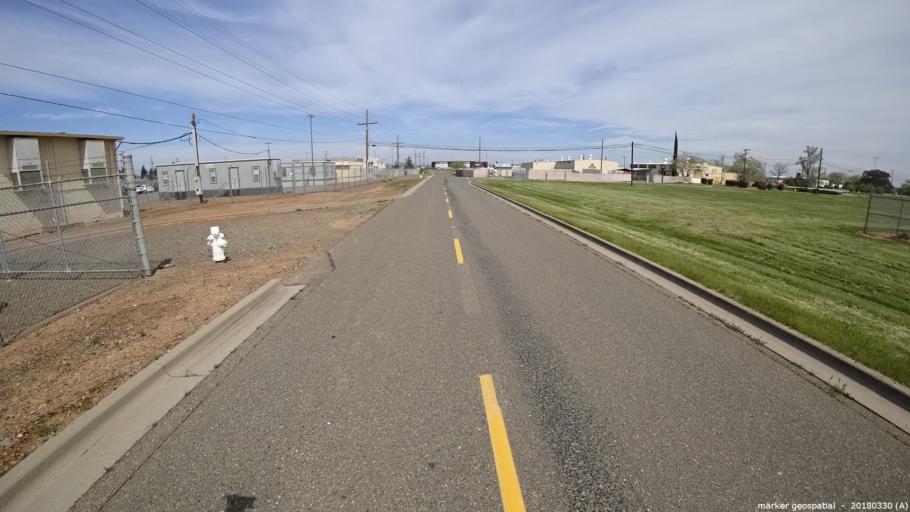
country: US
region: California
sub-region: Sacramento County
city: Rancho Cordova
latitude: 38.5586
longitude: -121.3141
